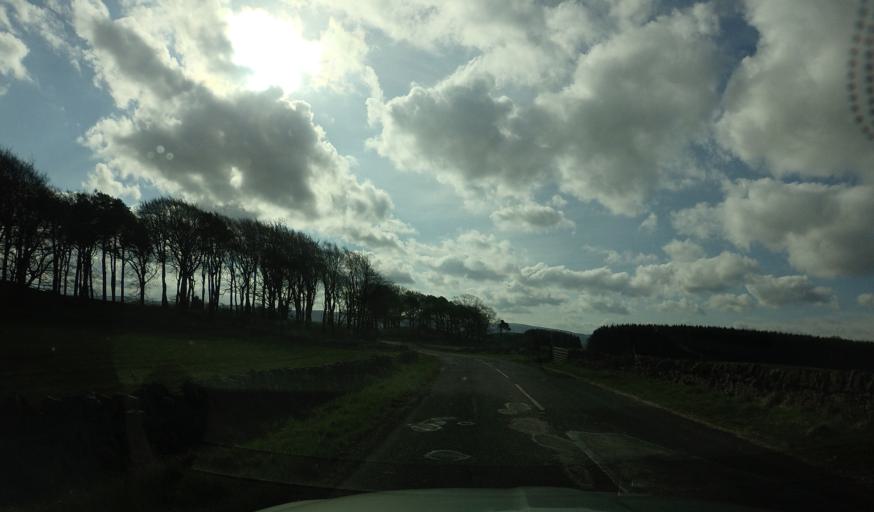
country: GB
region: Scotland
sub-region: Midlothian
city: Penicuik
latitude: 55.8025
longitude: -3.1722
